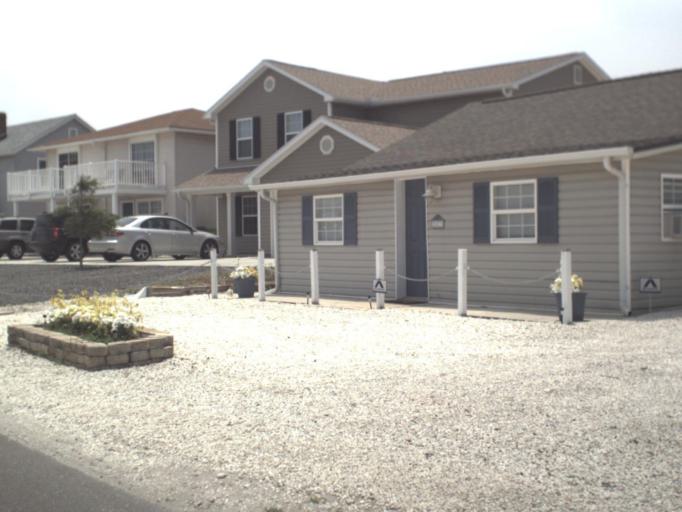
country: US
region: Florida
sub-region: Nassau County
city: Fernandina Beach
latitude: 30.6311
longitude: -81.4387
